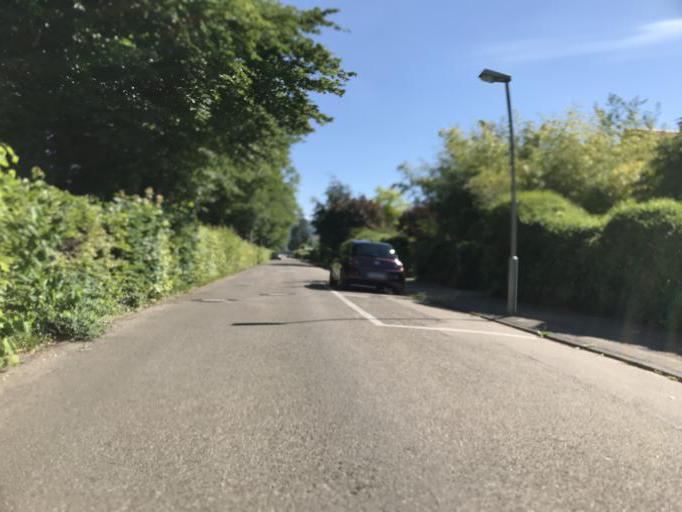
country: DE
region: Baden-Wuerttemberg
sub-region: Freiburg Region
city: Schopfheim
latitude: 47.6507
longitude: 7.8285
